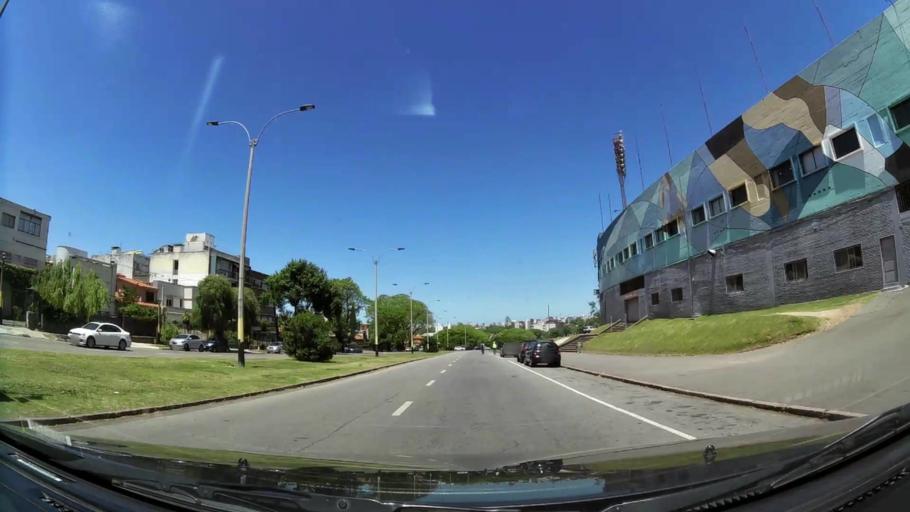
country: UY
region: Montevideo
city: Montevideo
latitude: -34.8943
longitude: -56.1511
